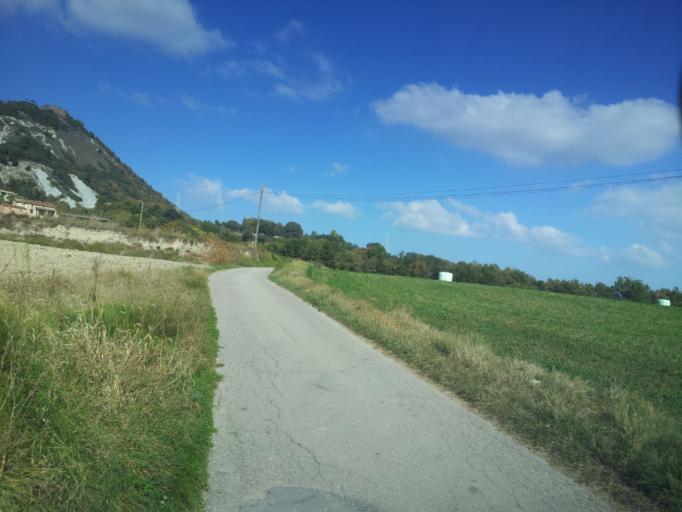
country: ES
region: Catalonia
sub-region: Provincia de Barcelona
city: Gurb
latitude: 41.9429
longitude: 2.2140
